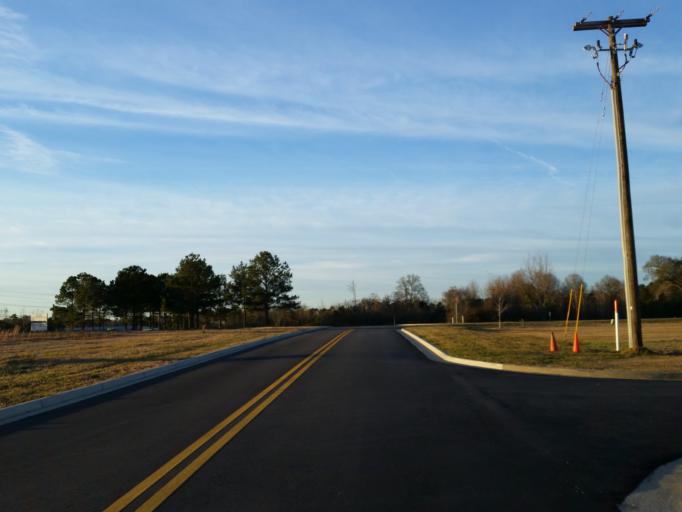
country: US
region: Georgia
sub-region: Tift County
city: Tifton
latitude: 31.4458
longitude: -83.5450
